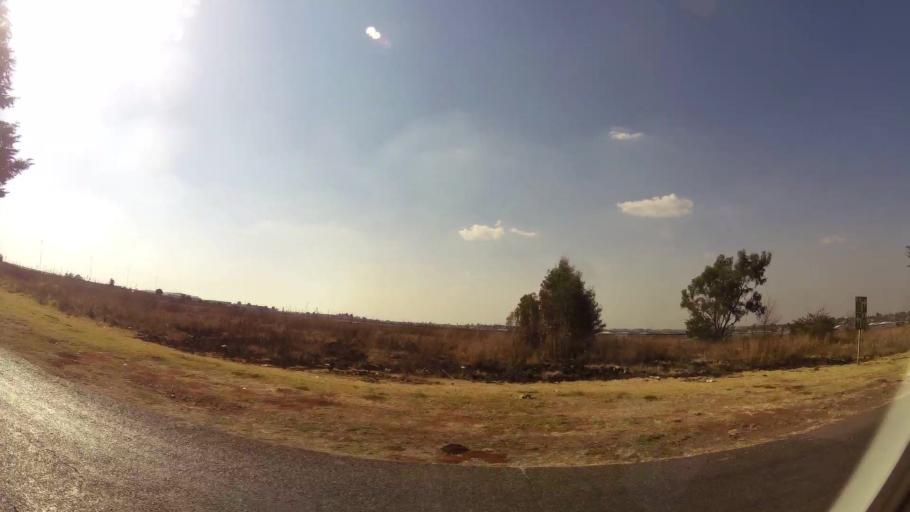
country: ZA
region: Gauteng
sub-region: Ekurhuleni Metropolitan Municipality
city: Boksburg
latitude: -26.2421
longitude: 28.2951
